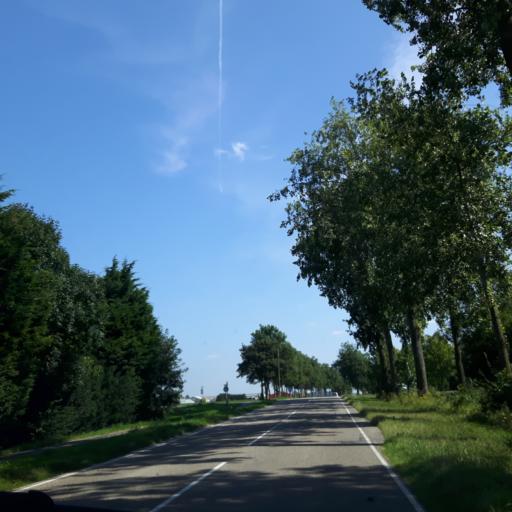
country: NL
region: North Brabant
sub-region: Gemeente Steenbergen
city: Nieuw-Vossemeer
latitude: 51.6209
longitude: 4.1648
